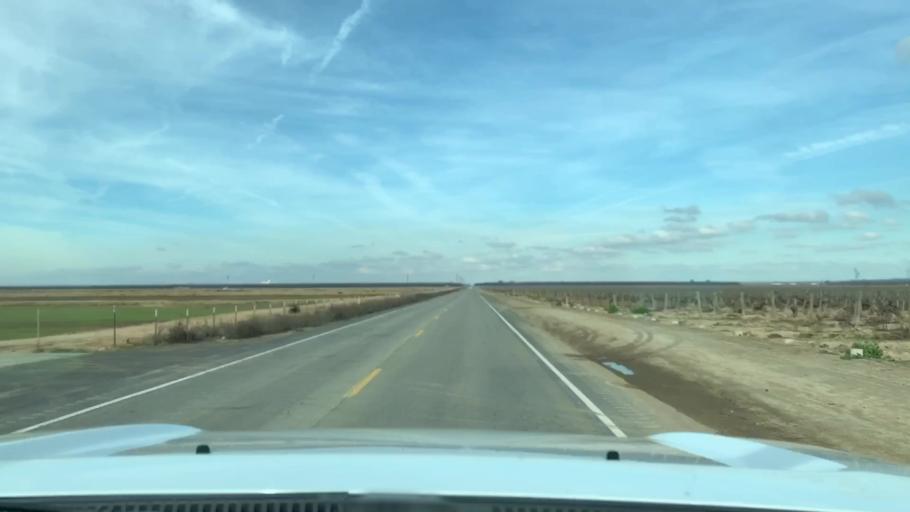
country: US
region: California
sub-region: Kern County
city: Rosedale
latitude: 35.4573
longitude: -119.1538
